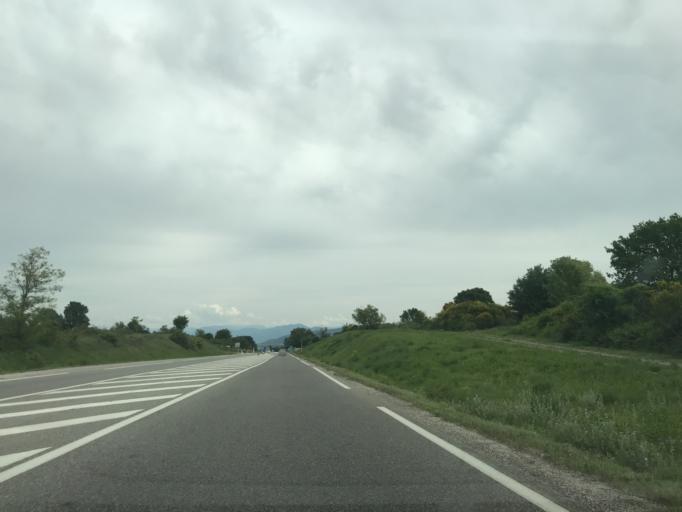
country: FR
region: Provence-Alpes-Cote d'Azur
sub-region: Departement des Alpes-de-Haute-Provence
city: Oraison
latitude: 43.9568
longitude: 5.8949
